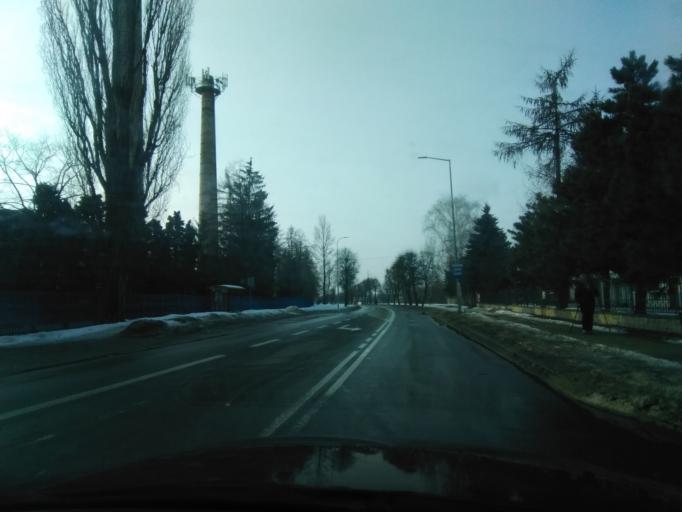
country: PL
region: Subcarpathian Voivodeship
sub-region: Krosno
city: Krosno
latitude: 49.7005
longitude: 21.7415
